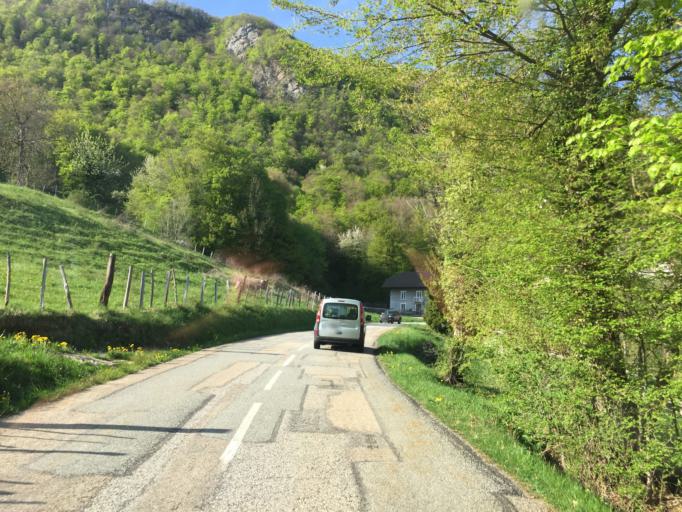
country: FR
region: Rhone-Alpes
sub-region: Departement de la Savoie
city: Frontenex
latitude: 45.6655
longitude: 6.3017
